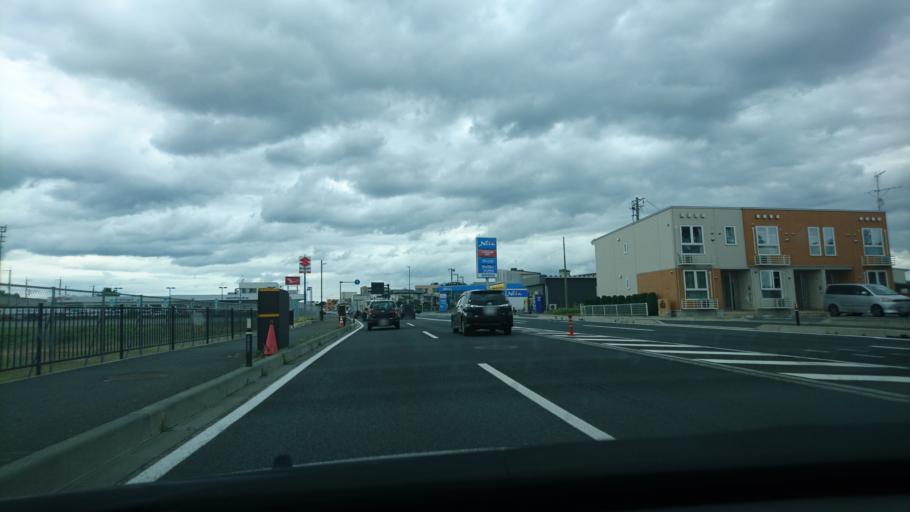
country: JP
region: Iwate
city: Morioka-shi
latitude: 39.7394
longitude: 141.1271
